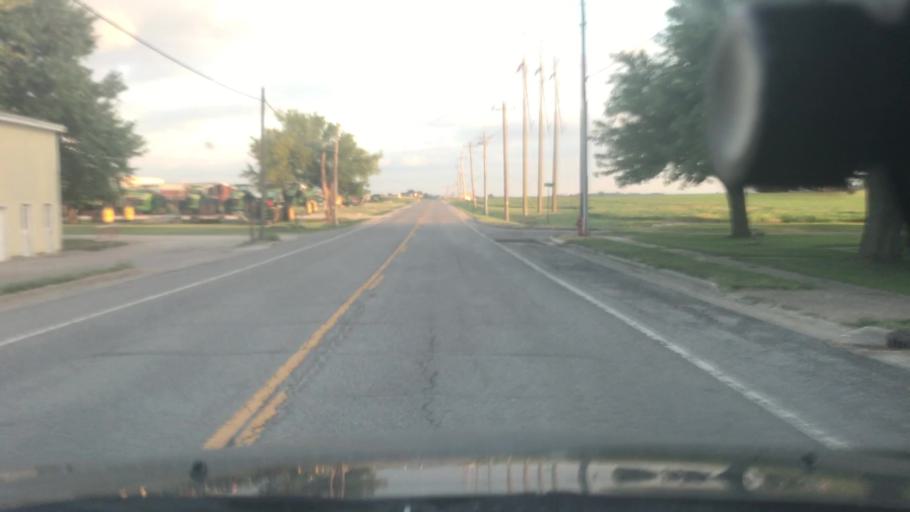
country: US
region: Illinois
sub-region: Washington County
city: Okawville
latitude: 38.4218
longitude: -89.5506
